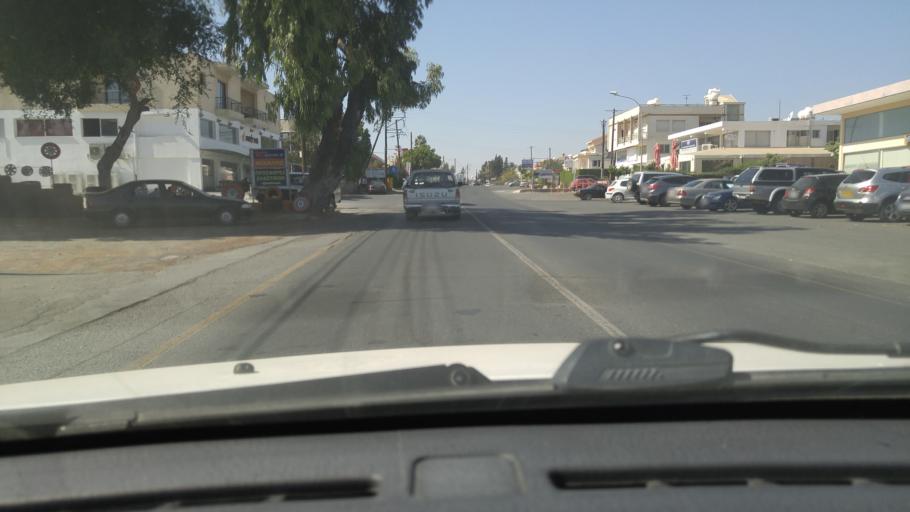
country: CY
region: Limassol
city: Ypsonas
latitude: 34.6828
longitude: 32.9684
